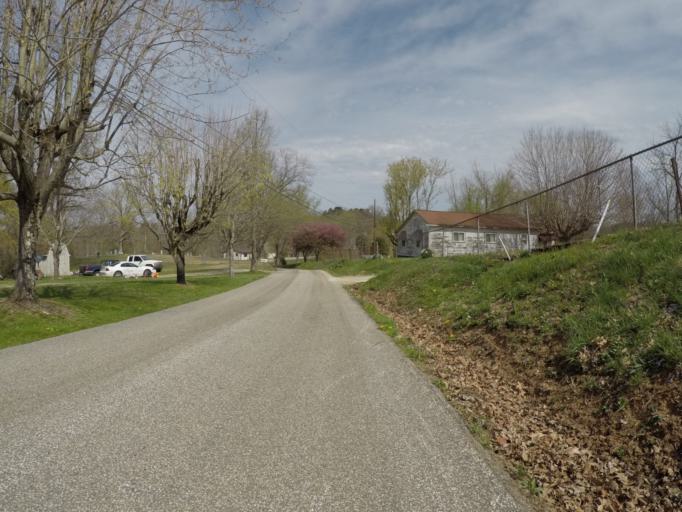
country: US
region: West Virginia
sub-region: Wayne County
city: Lavalette
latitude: 38.3347
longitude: -82.3628
